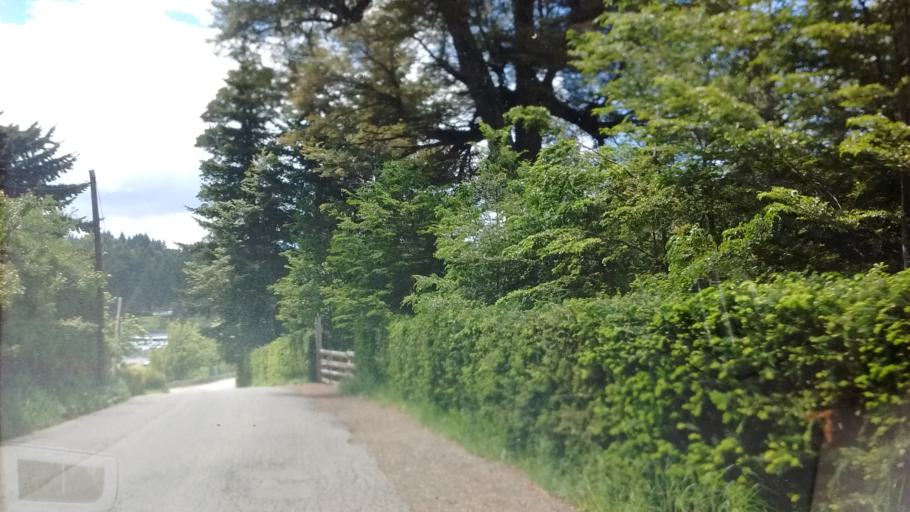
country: AR
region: Rio Negro
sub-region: Departamento de Bariloche
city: San Carlos de Bariloche
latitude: -41.0541
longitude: -71.5349
